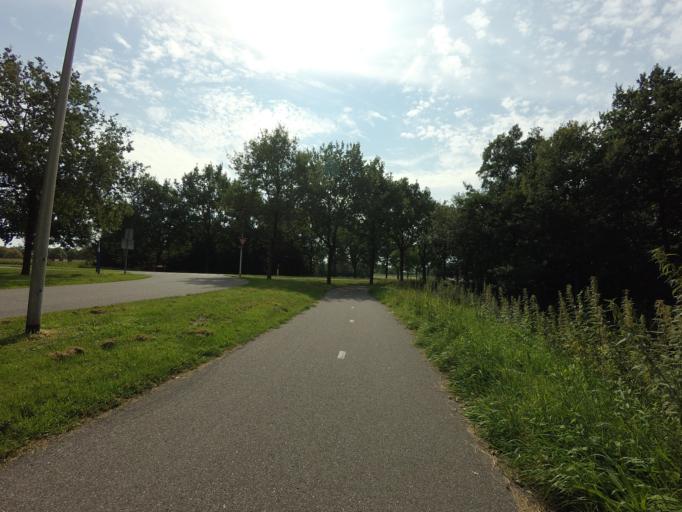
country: NL
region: Drenthe
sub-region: Gemeente Hoogeveen
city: Hoogeveen
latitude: 52.7137
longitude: 6.5350
